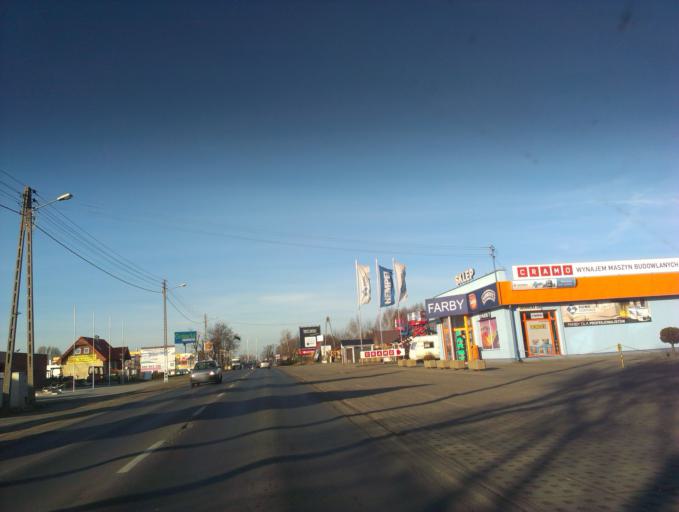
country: PL
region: Greater Poland Voivodeship
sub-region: Powiat poznanski
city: Suchy Las
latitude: 52.4593
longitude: 16.8949
